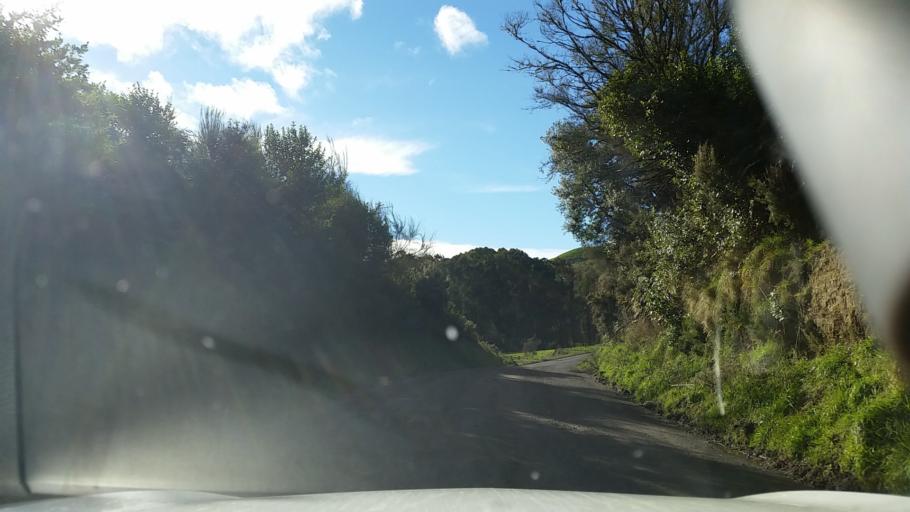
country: NZ
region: Bay of Plenty
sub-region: Rotorua District
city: Rotorua
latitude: -38.3586
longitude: 176.2127
